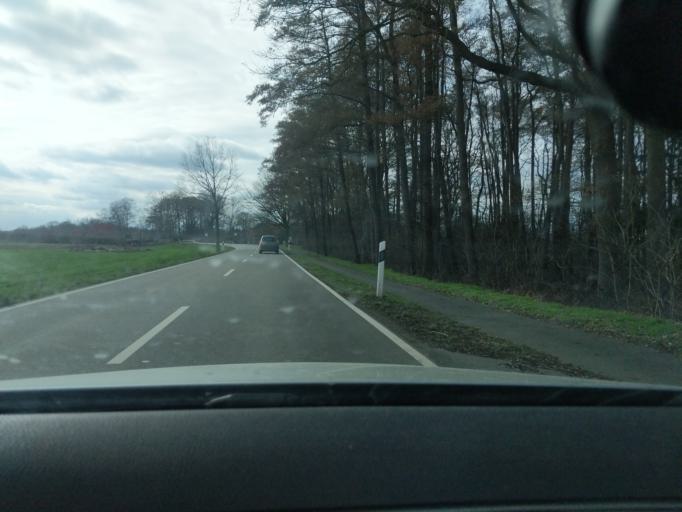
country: DE
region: Lower Saxony
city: Engelschoff
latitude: 53.6399
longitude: 9.3317
